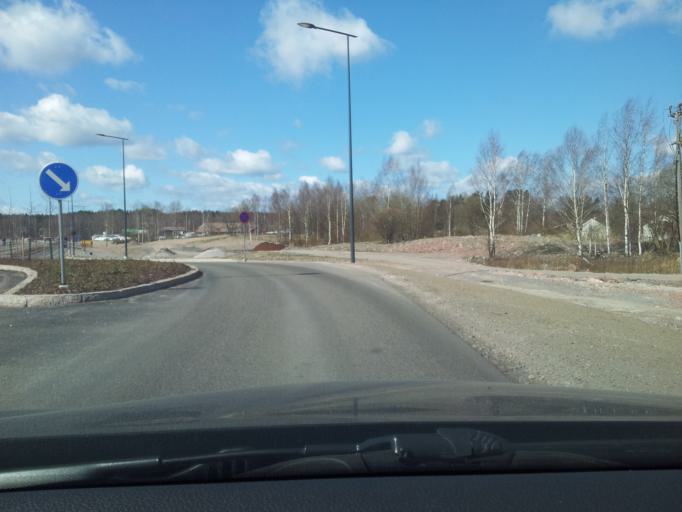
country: FI
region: Uusimaa
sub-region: Helsinki
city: Koukkuniemi
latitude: 60.1530
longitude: 24.7059
